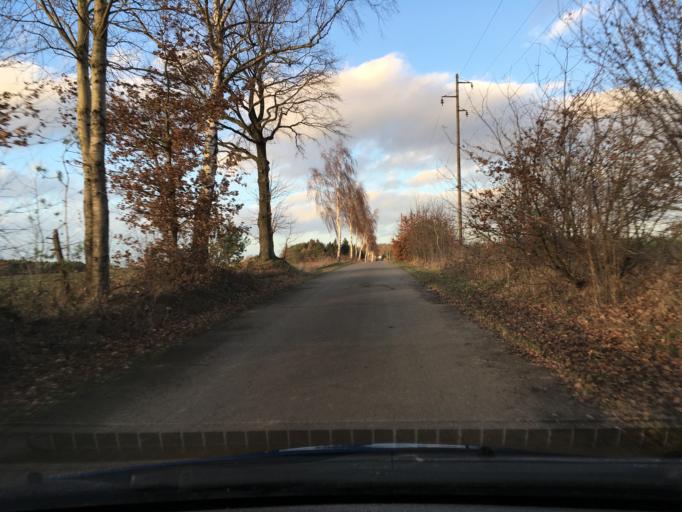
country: DE
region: Lower Saxony
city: Soderstorf
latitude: 53.1168
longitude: 10.1678
